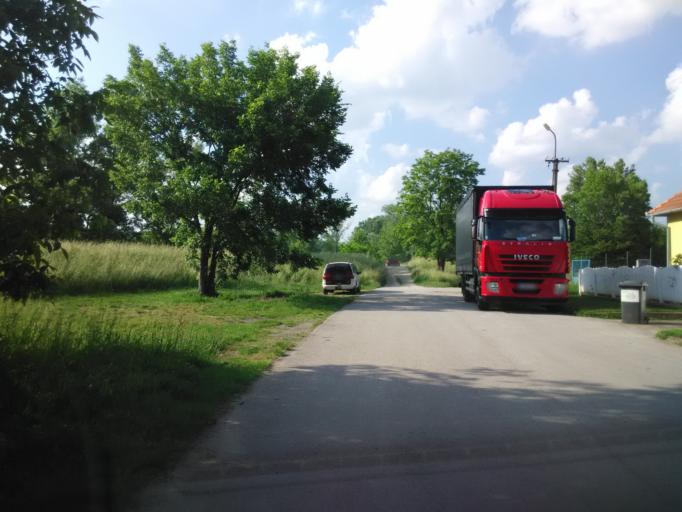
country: SK
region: Nitriansky
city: Tlmace
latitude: 48.2940
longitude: 18.5313
